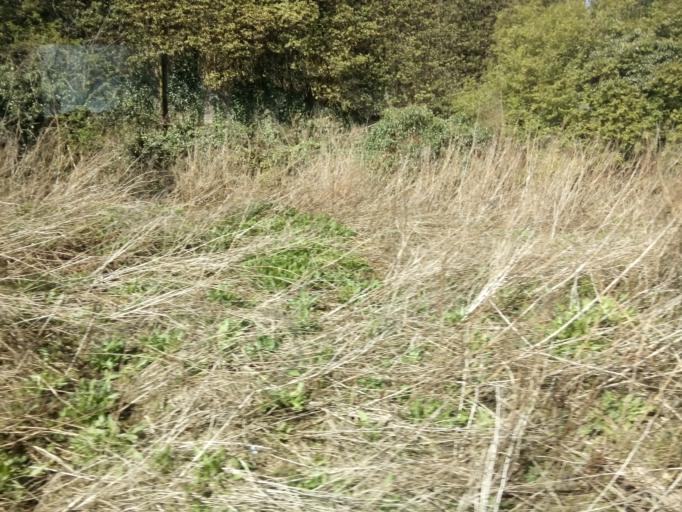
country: GB
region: Scotland
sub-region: Fife
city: Inverkeithing
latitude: 56.0333
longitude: -3.3952
